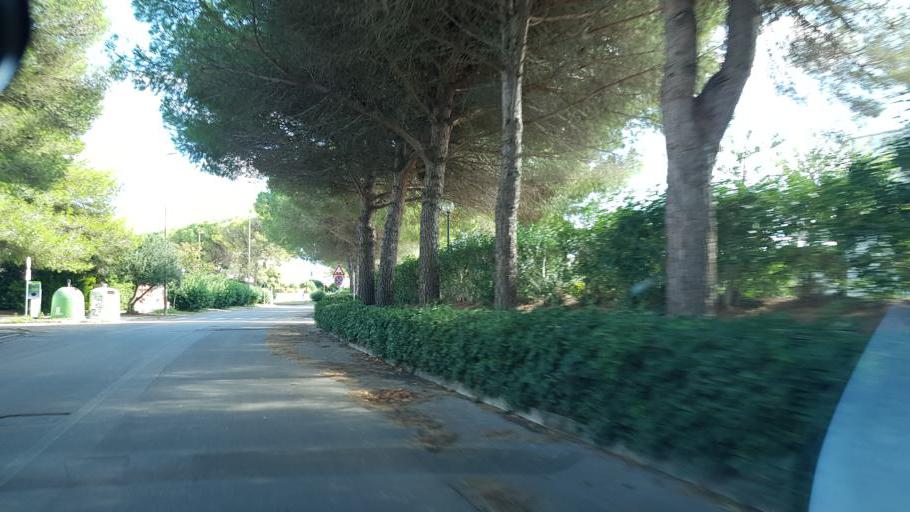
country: IT
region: Apulia
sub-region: Provincia di Lecce
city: Borgagne
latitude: 40.2720
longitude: 18.4242
